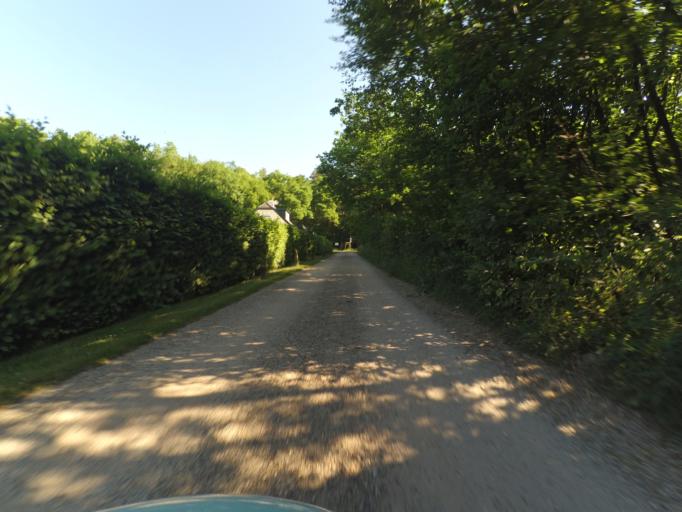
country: NL
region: Gelderland
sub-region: Gemeente Voorst
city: Voorst
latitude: 52.1843
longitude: 6.1447
